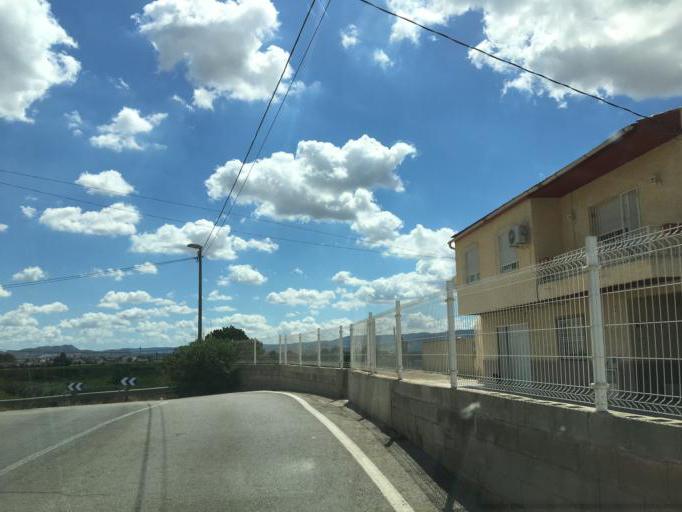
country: ES
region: Murcia
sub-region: Murcia
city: Santomera
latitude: 38.0509
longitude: -1.0673
